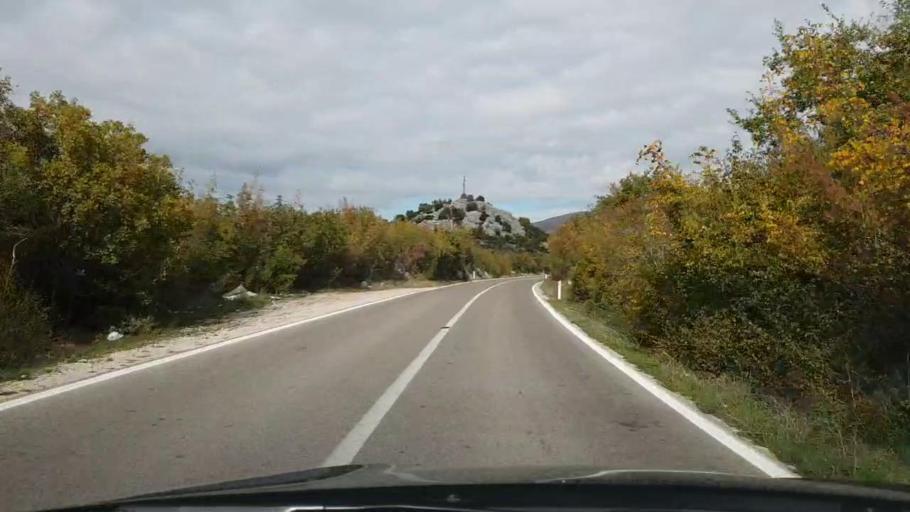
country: HR
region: Dubrovacko-Neretvanska
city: Cibaca
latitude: 42.6816
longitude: 18.2454
